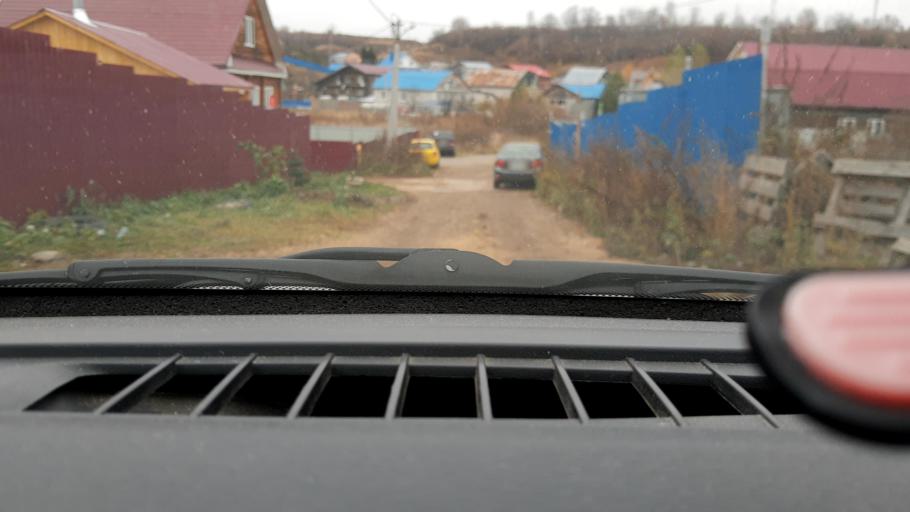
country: RU
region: Nizjnij Novgorod
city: Burevestnik
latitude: 56.1898
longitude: 43.9166
